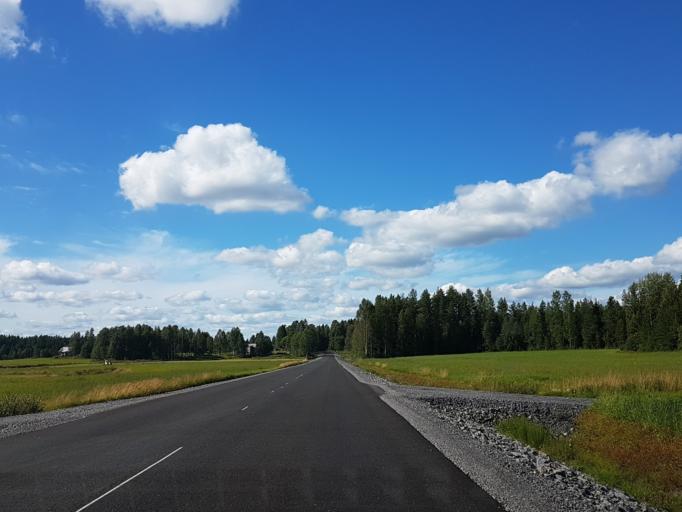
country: SE
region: Vaesterbotten
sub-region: Robertsfors Kommun
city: Robertsfors
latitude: 64.1354
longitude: 20.6319
